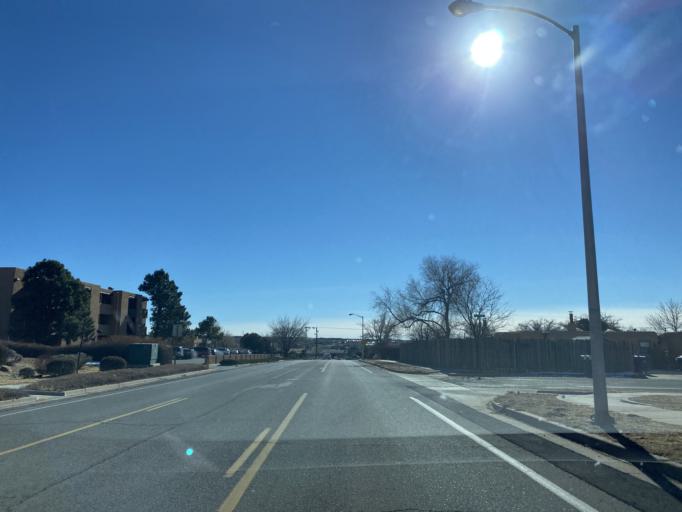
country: US
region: New Mexico
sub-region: Santa Fe County
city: Santa Fe
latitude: 35.6536
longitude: -105.9585
